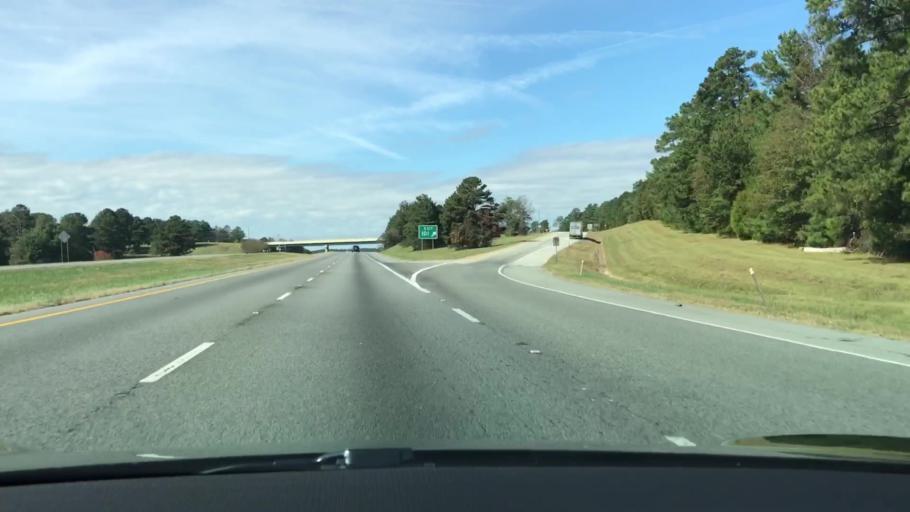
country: US
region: Georgia
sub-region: Walton County
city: Social Circle
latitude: 33.6088
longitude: -83.6947
